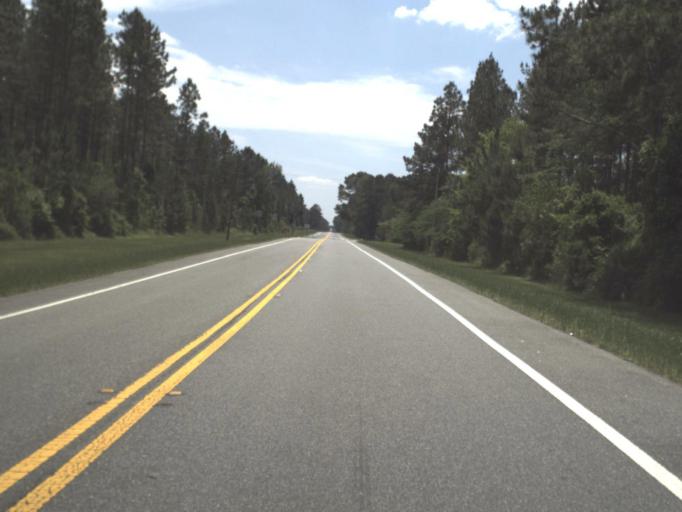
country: US
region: Florida
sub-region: Calhoun County
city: Blountstown
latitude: 30.3291
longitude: -85.1269
